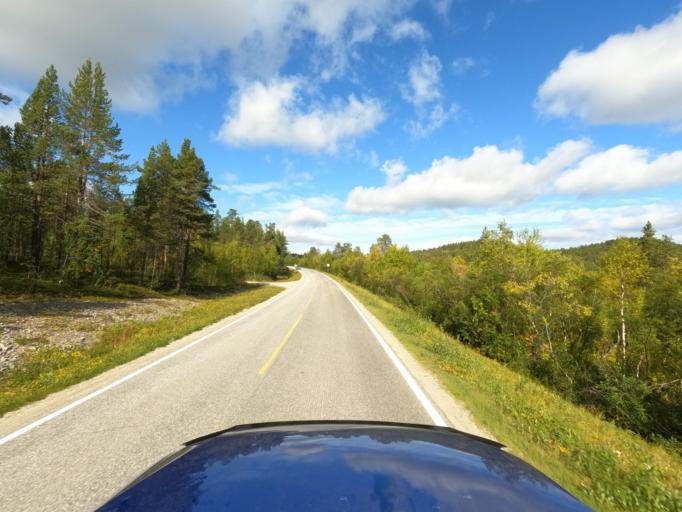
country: NO
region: Finnmark Fylke
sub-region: Karasjok
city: Karasjohka
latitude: 69.4801
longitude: 25.5169
